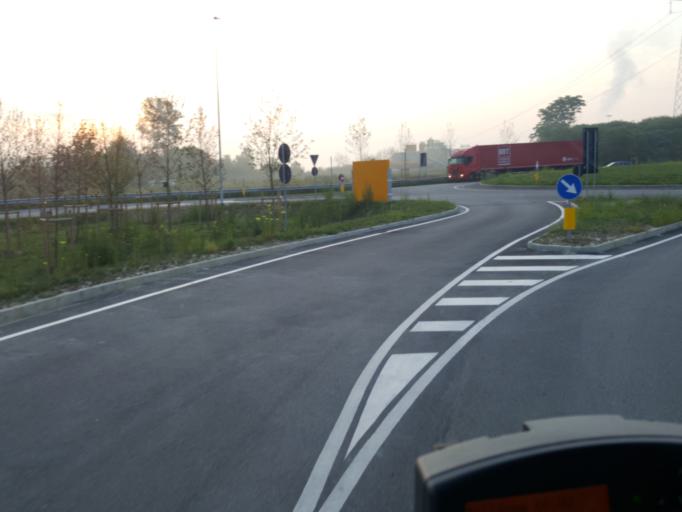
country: IT
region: Piedmont
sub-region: Provincia di Torino
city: Torrazza Piemonte
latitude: 45.2315
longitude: 7.9804
